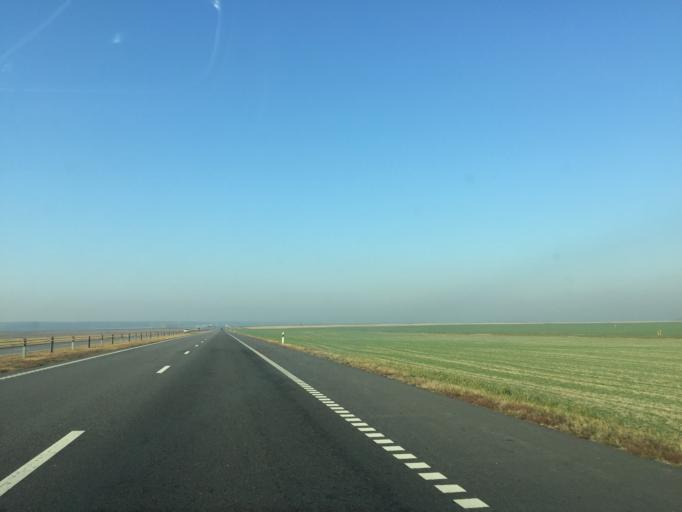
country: BY
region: Gomel
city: Kastsyukowka
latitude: 52.4877
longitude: 30.7961
